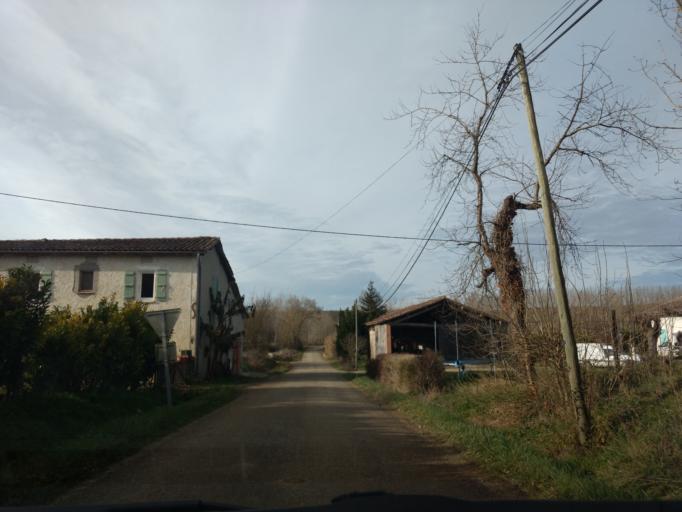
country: FR
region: Midi-Pyrenees
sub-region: Departement du Gers
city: Aubiet
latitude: 43.6716
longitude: 0.8029
